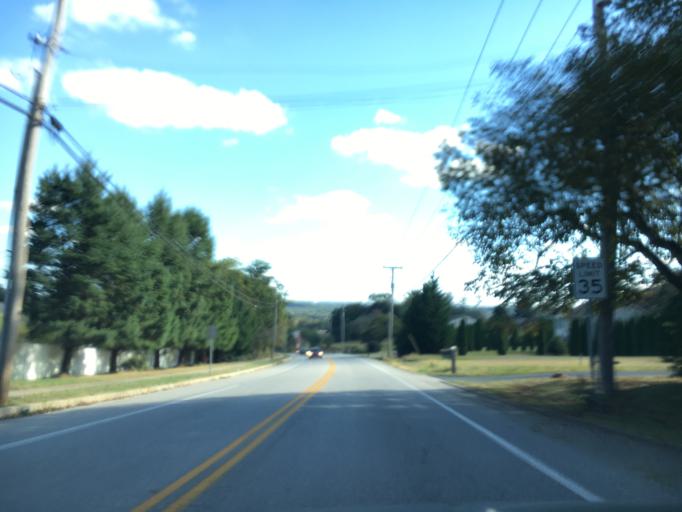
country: US
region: Pennsylvania
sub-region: York County
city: East York
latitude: 39.9965
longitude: -76.6761
